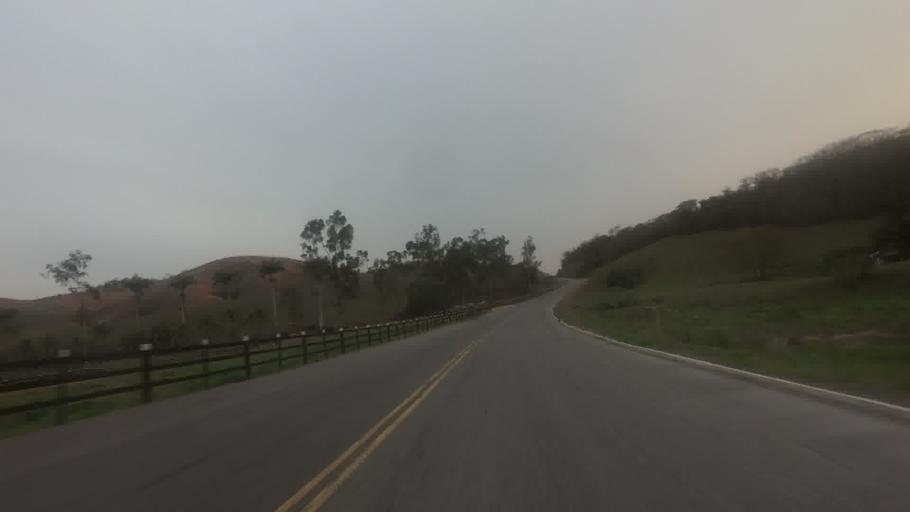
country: BR
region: Minas Gerais
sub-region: Recreio
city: Recreio
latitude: -21.7080
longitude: -42.4242
